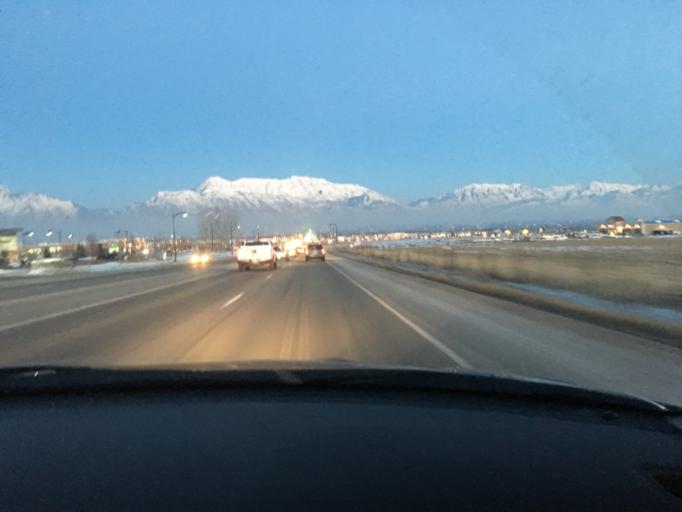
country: US
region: Utah
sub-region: Utah County
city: Saratoga Springs
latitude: 40.3875
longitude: -111.9264
